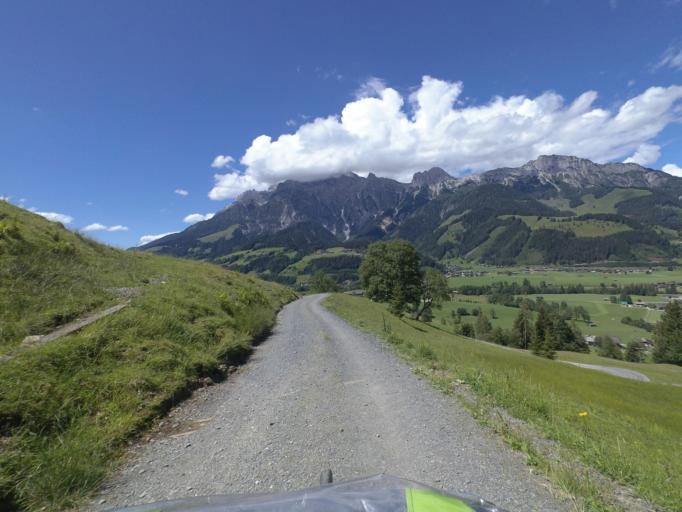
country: AT
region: Salzburg
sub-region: Politischer Bezirk Zell am See
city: Leogang
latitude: 47.4315
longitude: 12.7719
